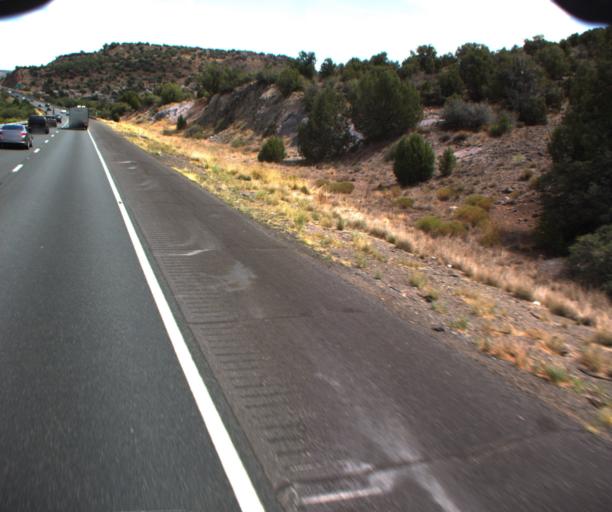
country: US
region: Arizona
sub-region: Yavapai County
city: Camp Verde
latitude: 34.4945
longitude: -112.0047
